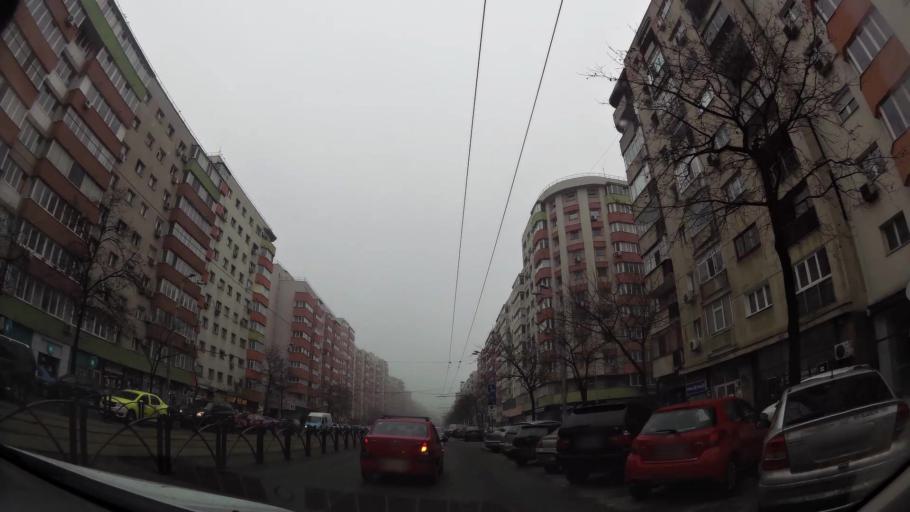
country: RO
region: Bucuresti
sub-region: Municipiul Bucuresti
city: Bucharest
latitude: 44.4408
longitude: 26.1171
